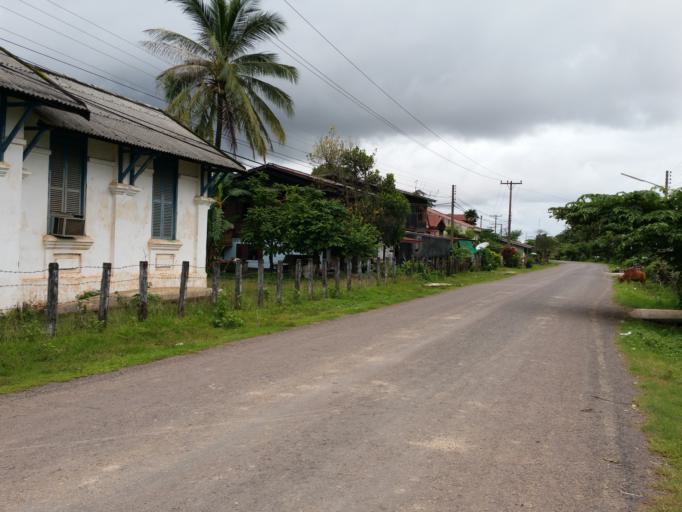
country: LA
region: Champasak
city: Champasak
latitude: 14.9065
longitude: 105.8845
